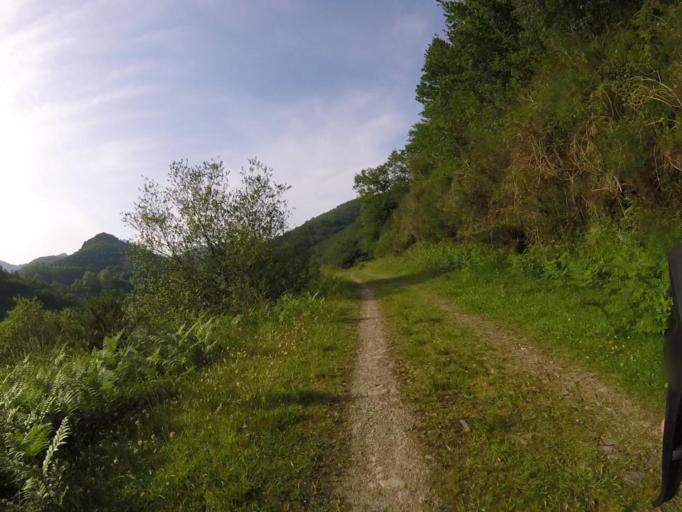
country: ES
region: Navarre
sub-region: Provincia de Navarra
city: Arano
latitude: 43.2272
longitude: -1.8659
